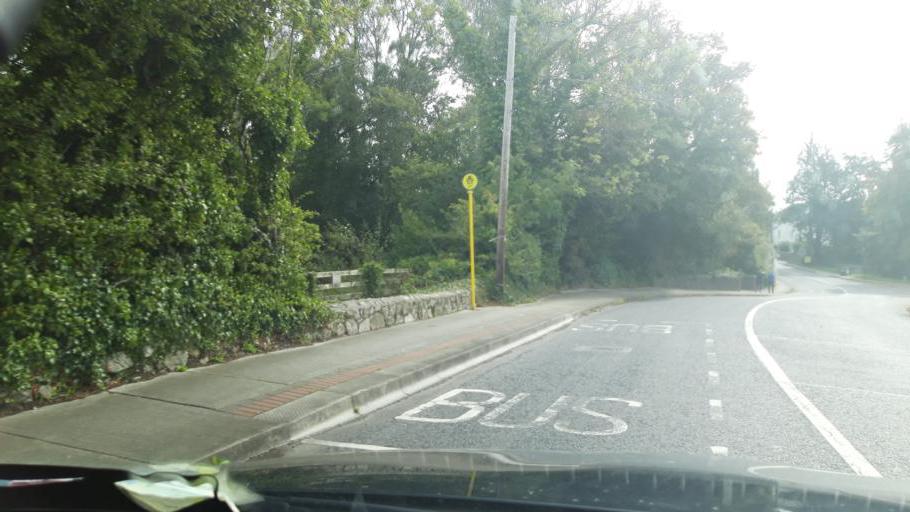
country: IE
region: Leinster
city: Foxrock
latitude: 53.2432
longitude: -6.1989
